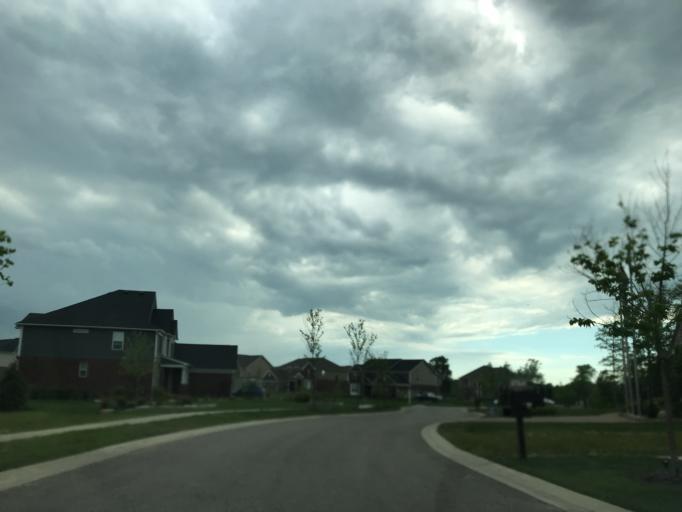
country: US
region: Michigan
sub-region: Oakland County
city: South Lyon
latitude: 42.4563
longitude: -83.5751
